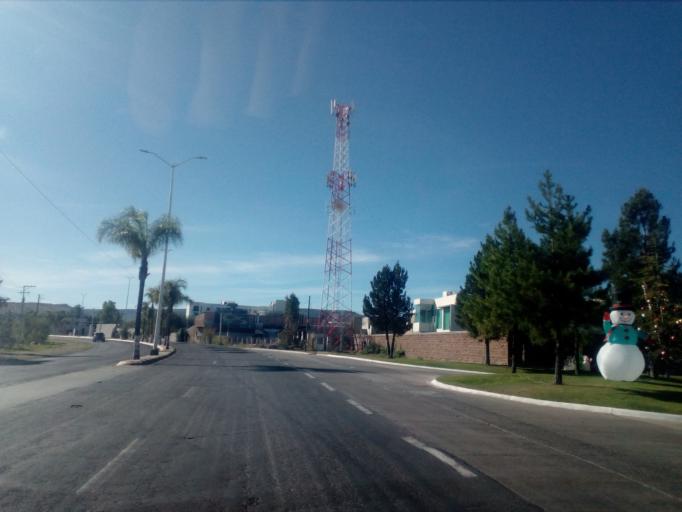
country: MX
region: Durango
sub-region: Durango
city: Sebastian Lerdo de Tejada
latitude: 23.9713
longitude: -104.6655
